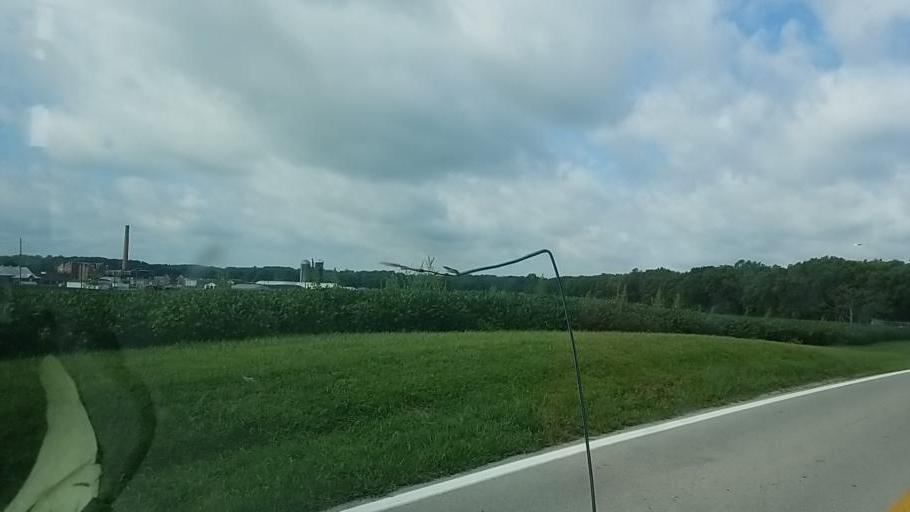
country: US
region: Ohio
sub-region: Franklin County
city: Grove City
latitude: 39.8032
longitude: -83.1554
